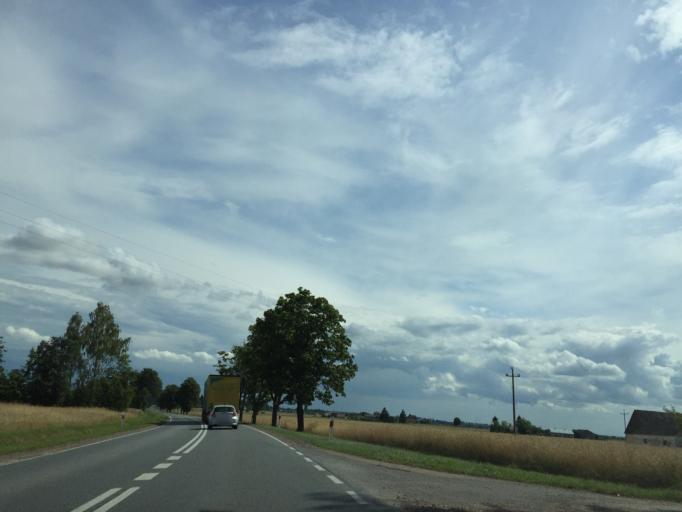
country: PL
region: Masovian Voivodeship
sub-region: Powiat losicki
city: Sarnaki
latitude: 52.2958
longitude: 22.8229
